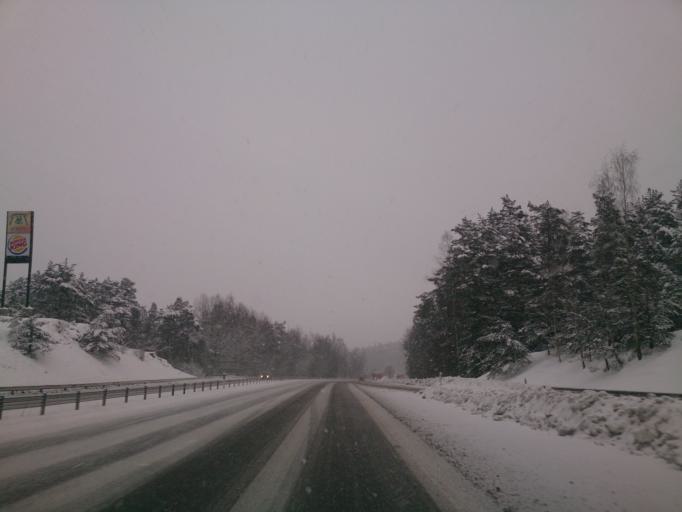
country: SE
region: Soedermanland
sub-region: Nykopings Kommun
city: Nykoping
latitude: 58.7646
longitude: 16.9917
